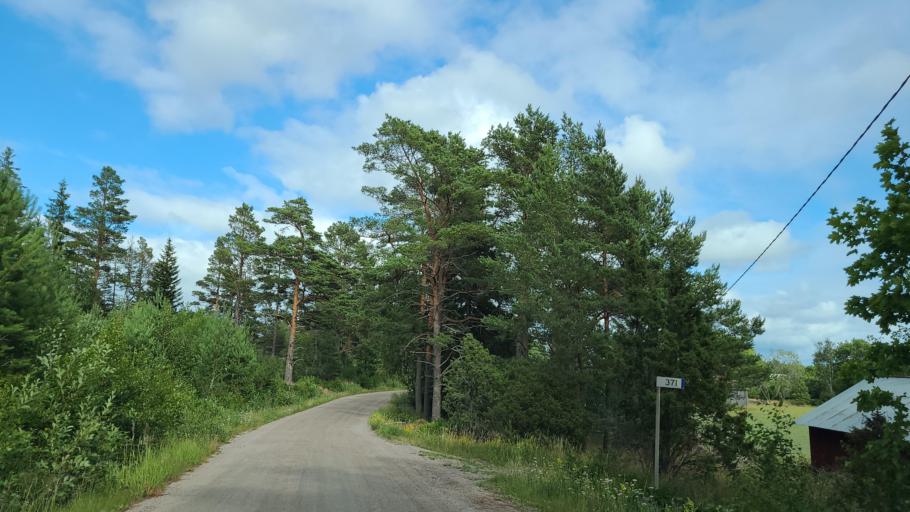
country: FI
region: Varsinais-Suomi
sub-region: Aboland-Turunmaa
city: Nagu
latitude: 60.1416
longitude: 21.7918
